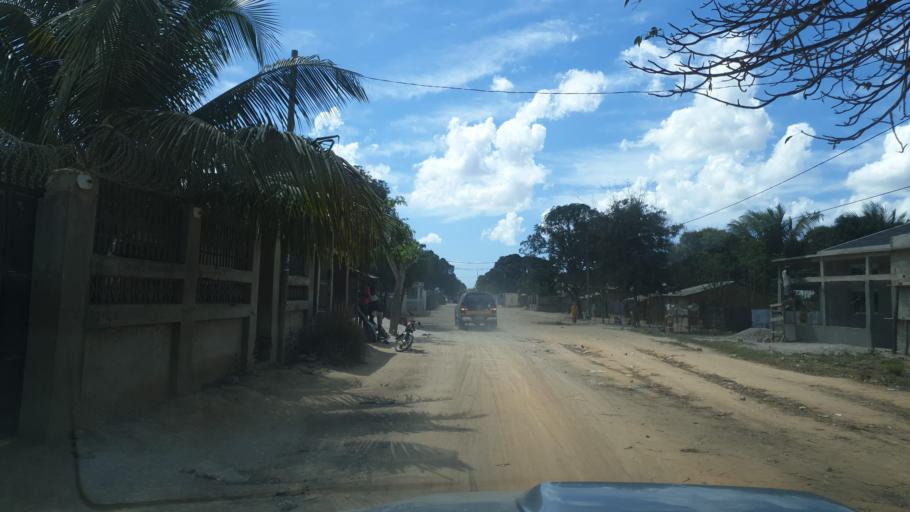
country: MZ
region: Nampula
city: Nacala
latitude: -14.5699
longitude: 40.6947
